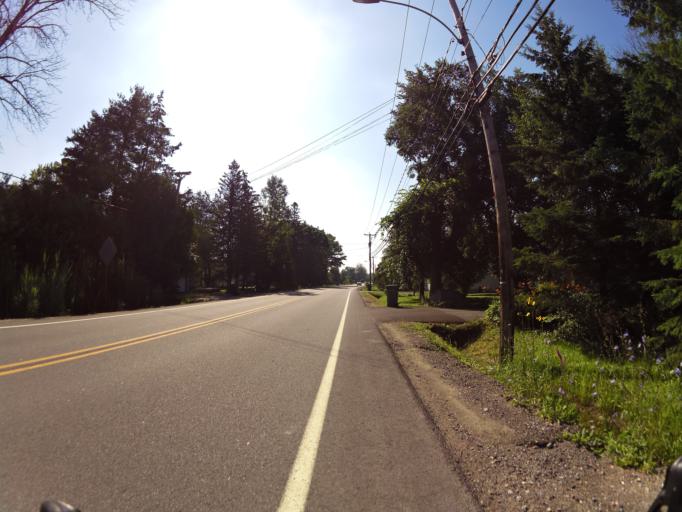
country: CA
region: Quebec
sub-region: Outaouais
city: Gatineau
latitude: 45.4960
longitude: -75.7770
